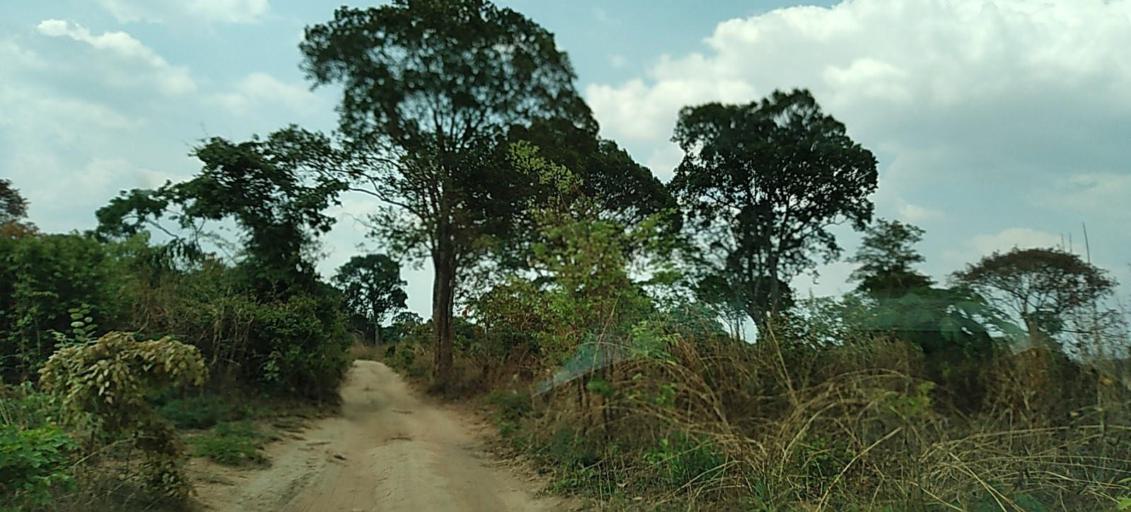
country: ZM
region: Copperbelt
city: Chililabombwe
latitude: -12.3242
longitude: 27.7487
